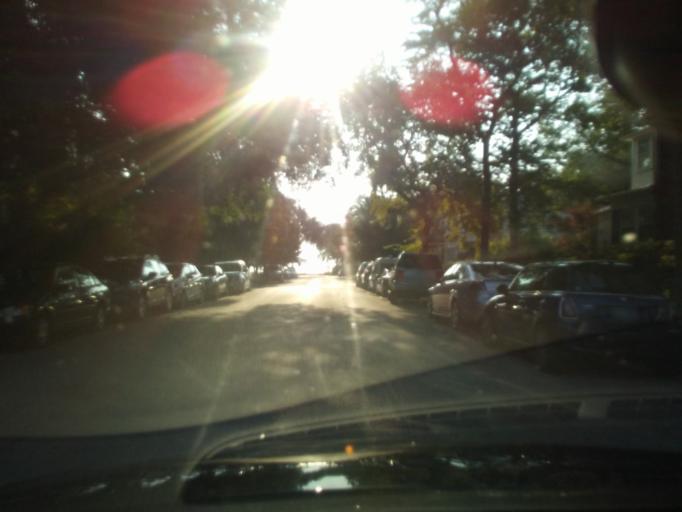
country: US
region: Illinois
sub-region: Cook County
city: Evanston
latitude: 42.0321
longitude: -87.6721
